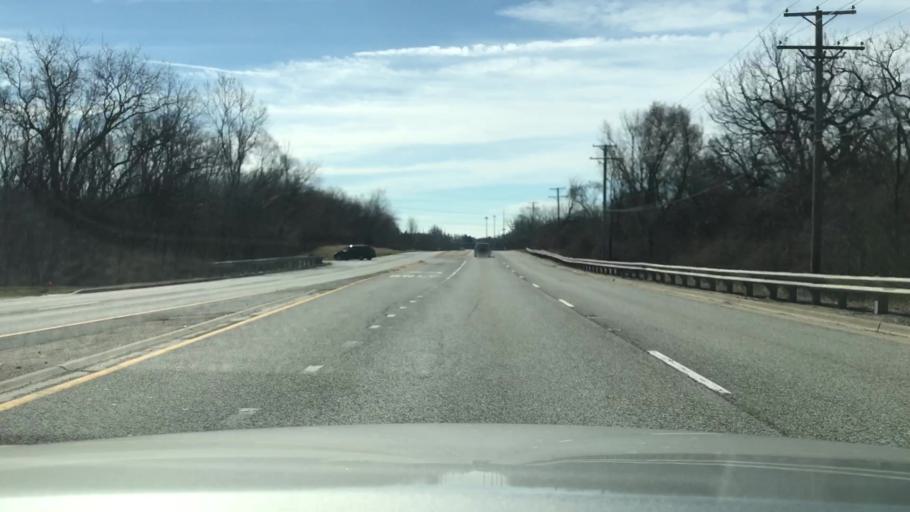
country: US
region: Illinois
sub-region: DuPage County
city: Woodridge
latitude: 41.7580
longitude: -88.0650
